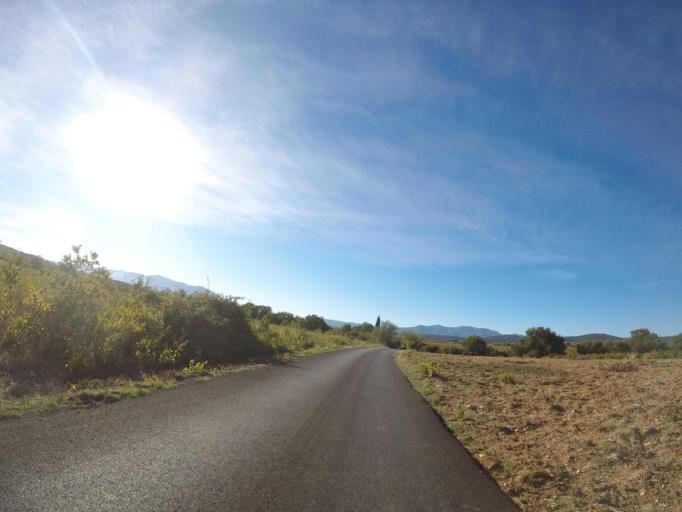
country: FR
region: Languedoc-Roussillon
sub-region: Departement des Pyrenees-Orientales
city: Llupia
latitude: 42.5952
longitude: 2.7639
